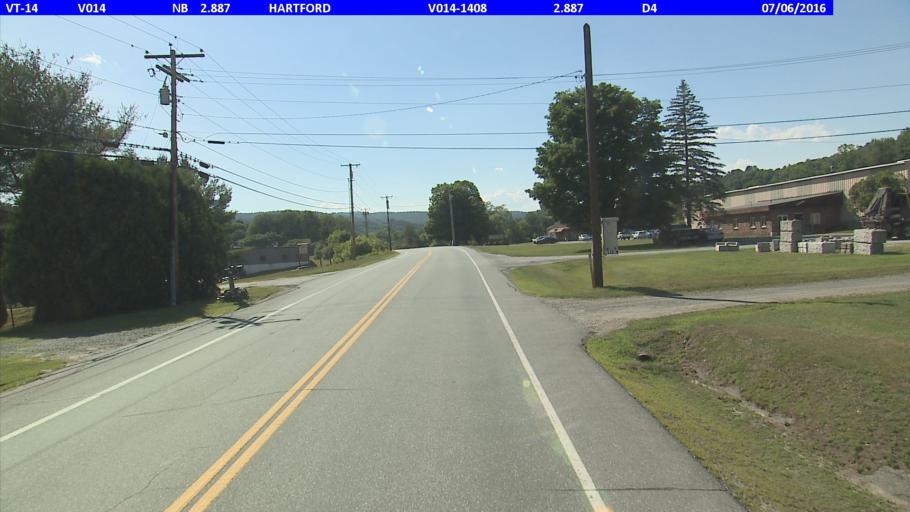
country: US
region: Vermont
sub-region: Windsor County
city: White River Junction
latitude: 43.6697
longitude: -72.3702
